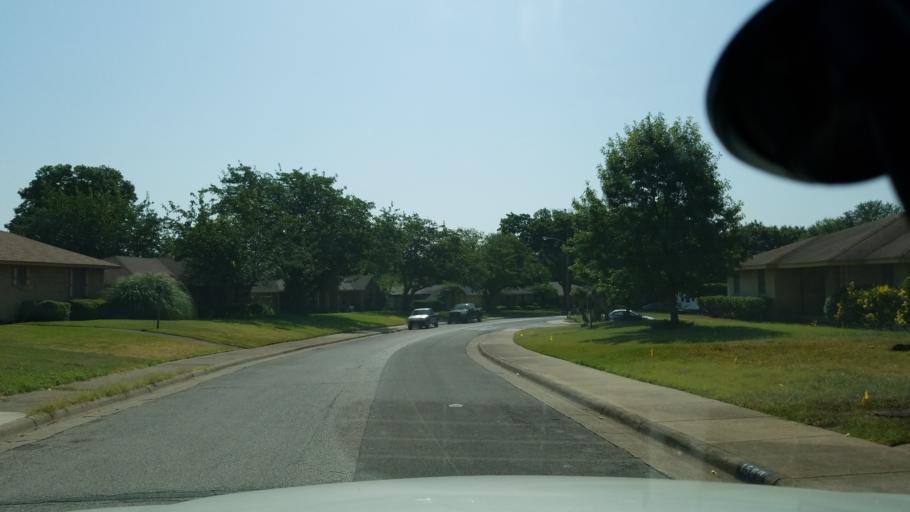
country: US
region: Texas
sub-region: Dallas County
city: Cockrell Hill
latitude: 32.6818
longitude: -96.8475
